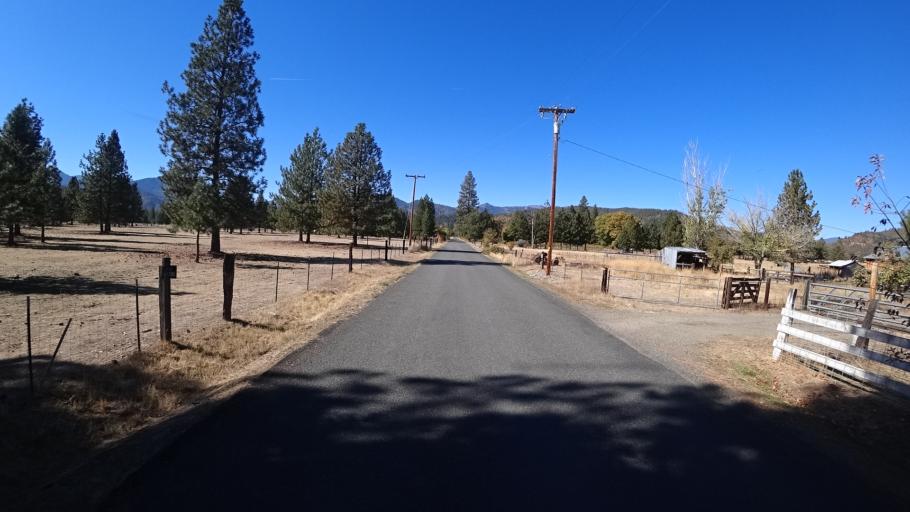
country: US
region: California
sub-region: Siskiyou County
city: Yreka
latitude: 41.5485
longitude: -122.9176
